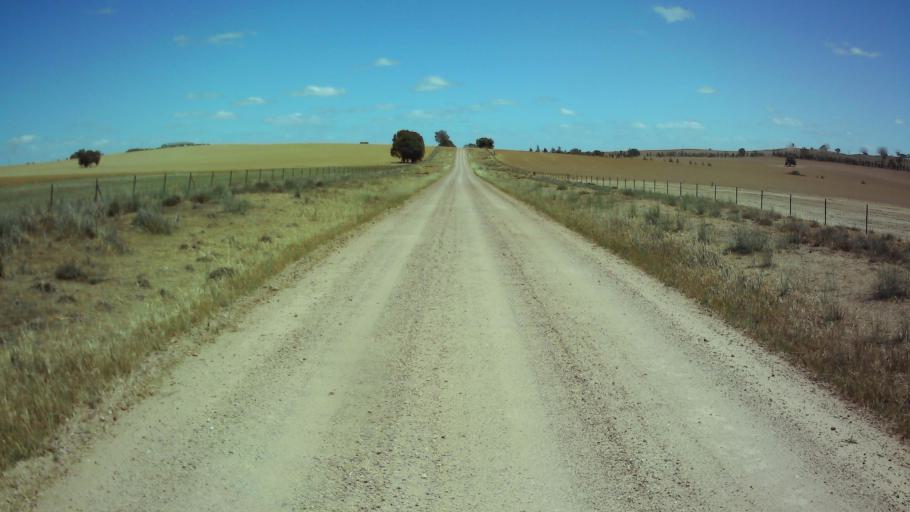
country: AU
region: New South Wales
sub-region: Weddin
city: Grenfell
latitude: -33.9446
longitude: 148.3295
